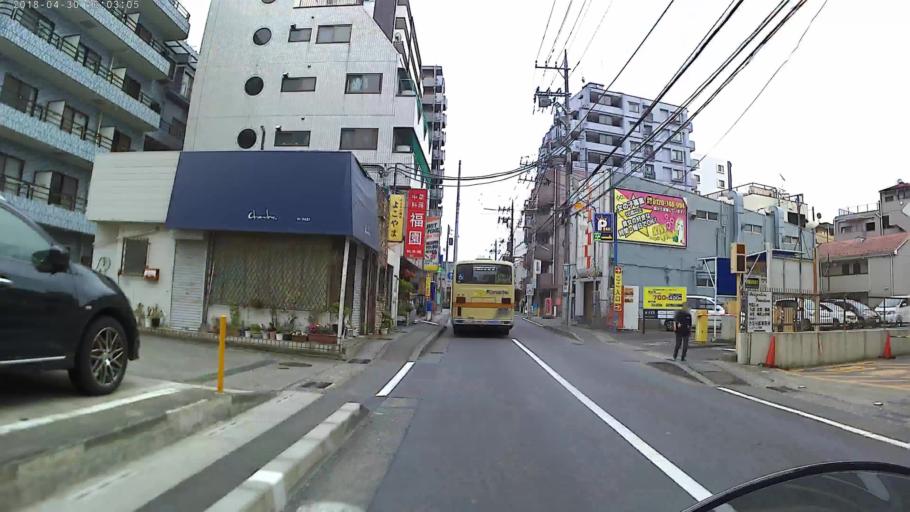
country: JP
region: Tokyo
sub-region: Machida-shi
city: Machida
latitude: 35.5137
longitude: 139.4216
